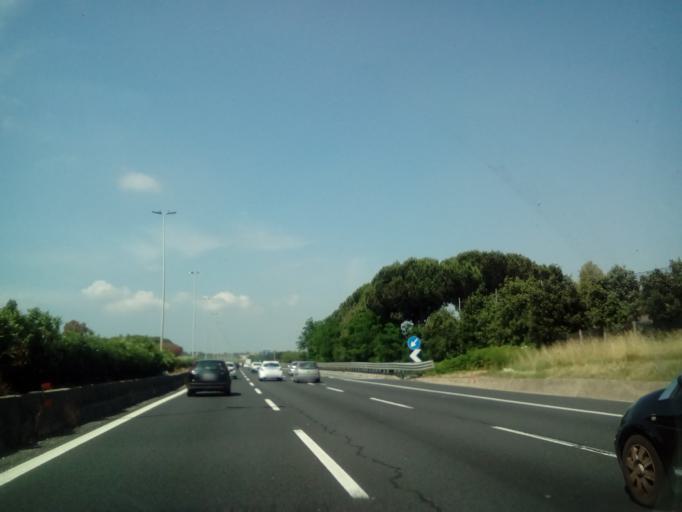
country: IT
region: Latium
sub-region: Citta metropolitana di Roma Capitale
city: Borgo Lotti
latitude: 41.7987
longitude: 12.5409
